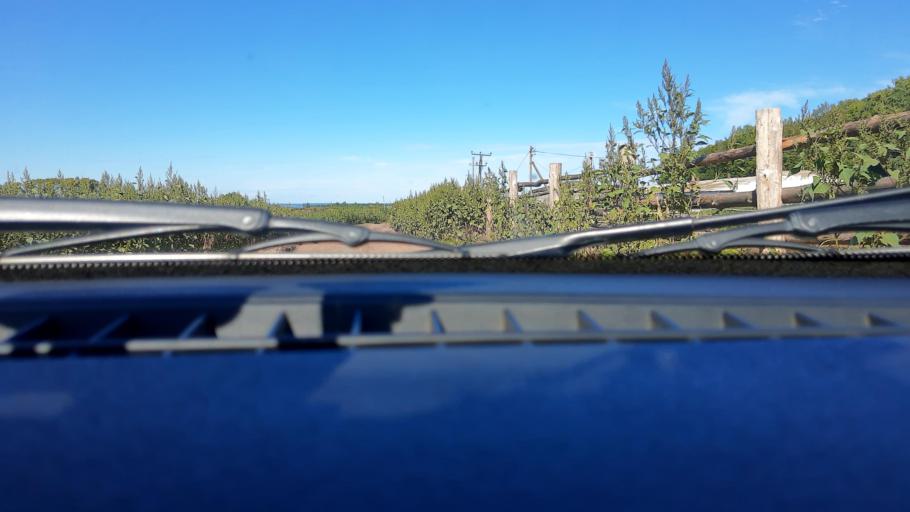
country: RU
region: Bashkortostan
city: Asanovo
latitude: 54.8181
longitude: 55.6224
